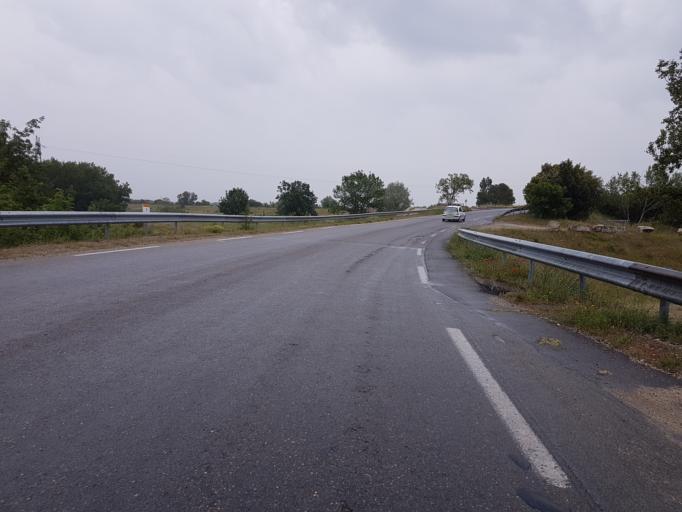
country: FR
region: Languedoc-Roussillon
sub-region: Departement du Gard
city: Sauveterre
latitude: 43.9967
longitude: 4.8141
